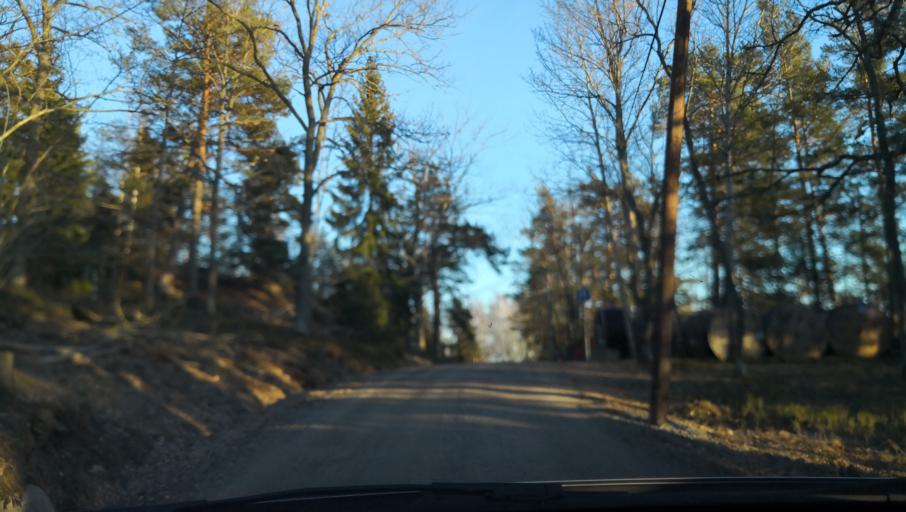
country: SE
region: Stockholm
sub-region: Varmdo Kommun
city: Mortnas
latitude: 59.3344
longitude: 18.4449
